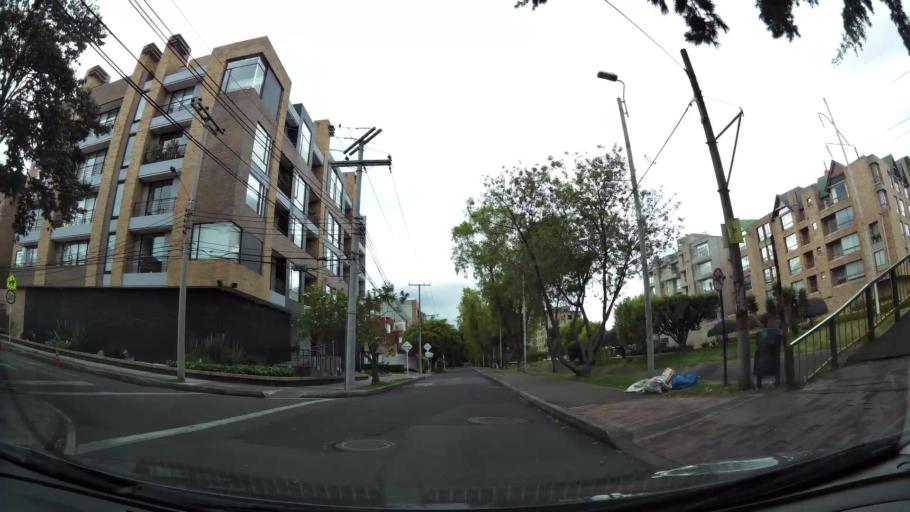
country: CO
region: Bogota D.C.
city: Barrio San Luis
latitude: 4.6955
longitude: -74.0480
